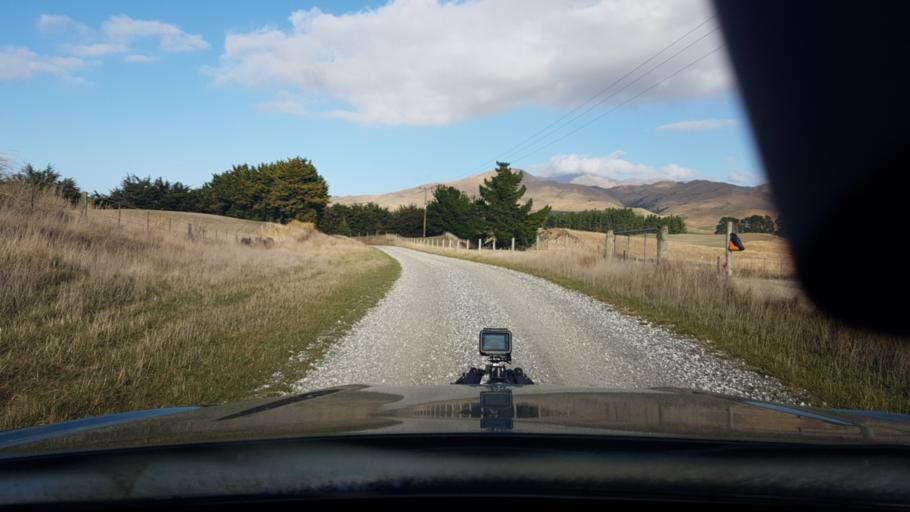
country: NZ
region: Marlborough
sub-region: Marlborough District
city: Blenheim
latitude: -41.8398
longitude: 174.1243
